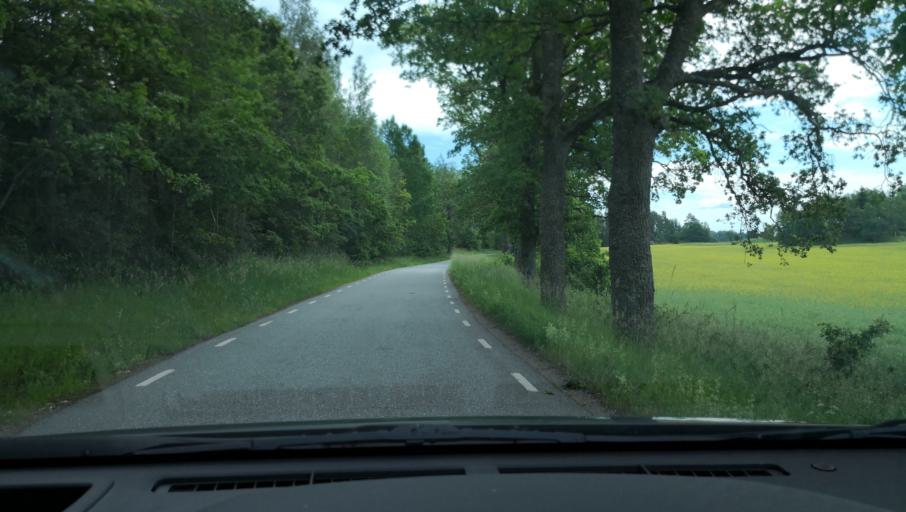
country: SE
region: Uppsala
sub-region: Enkopings Kommun
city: Orsundsbro
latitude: 59.7022
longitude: 17.4255
